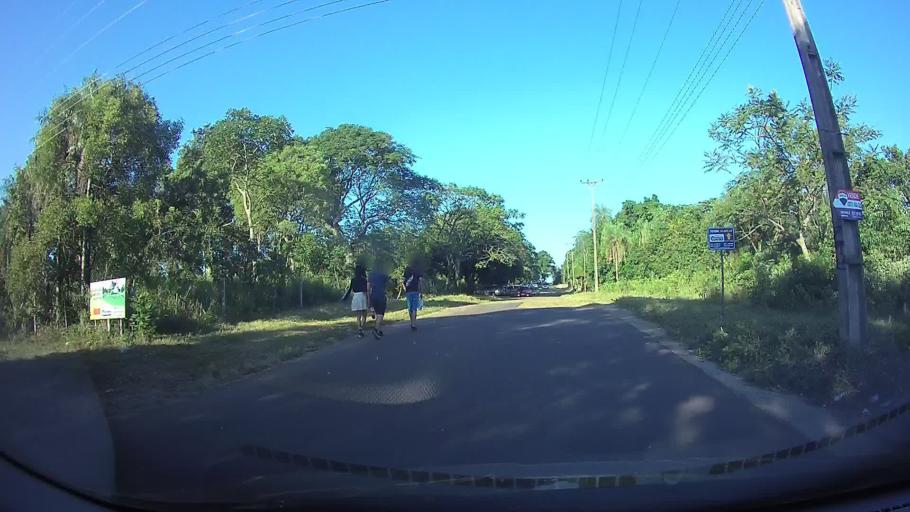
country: PY
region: Cordillera
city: San Bernardino
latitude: -25.3133
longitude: -57.2628
